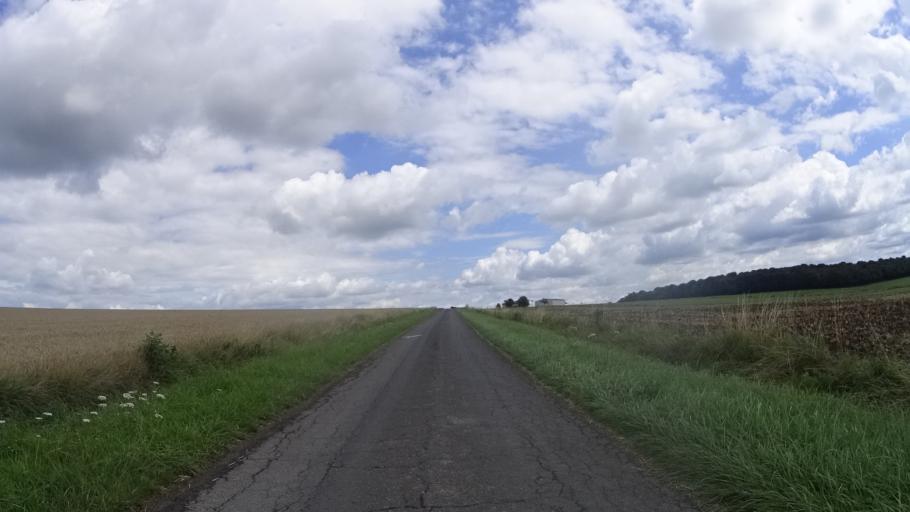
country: FR
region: Champagne-Ardenne
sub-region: Departement de la Haute-Marne
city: Montier-en-Der
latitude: 48.4918
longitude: 4.7579
